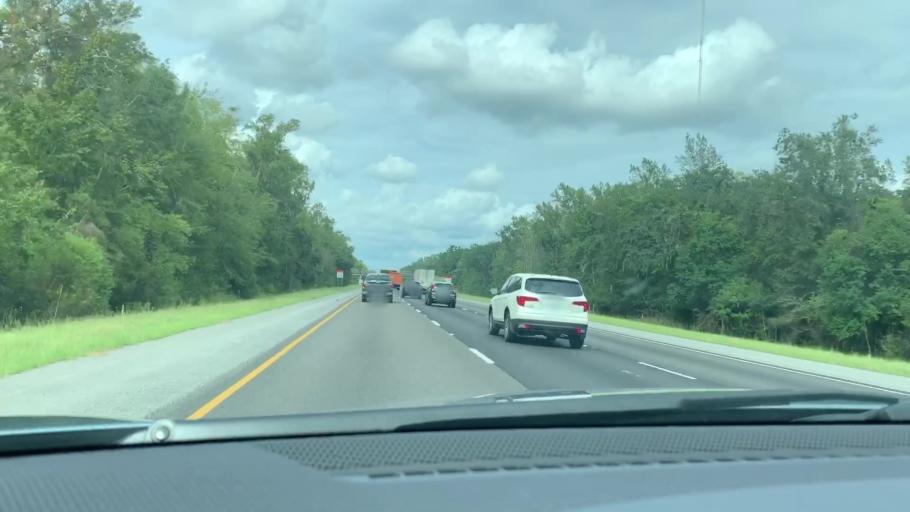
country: US
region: Georgia
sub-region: Liberty County
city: Midway
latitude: 31.6918
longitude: -81.3912
